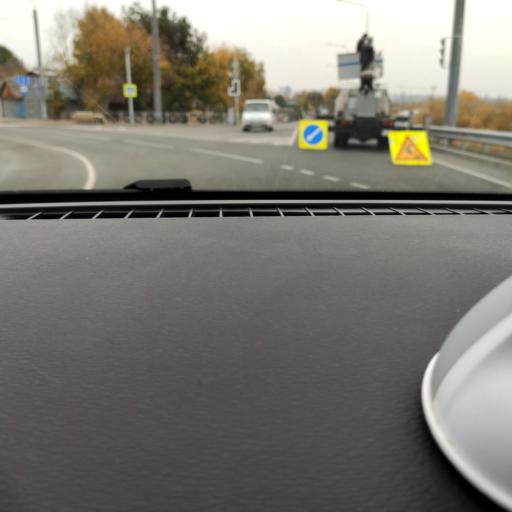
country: RU
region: Samara
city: Rozhdestveno
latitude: 53.1786
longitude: 50.0866
